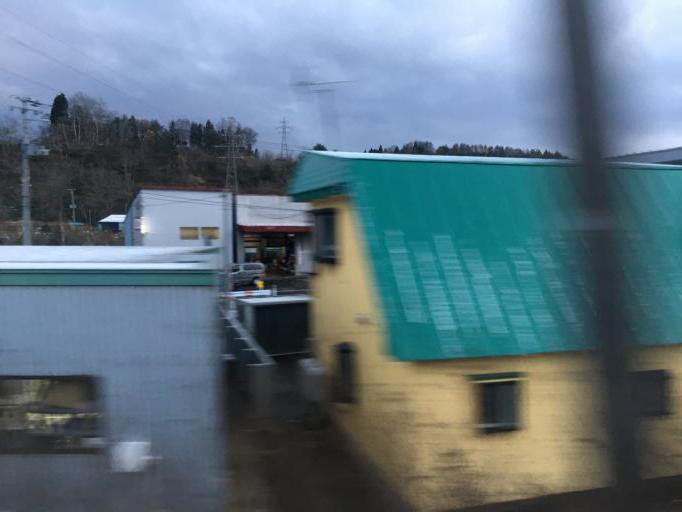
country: JP
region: Aomori
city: Aomori Shi
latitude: 40.8256
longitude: 140.6631
